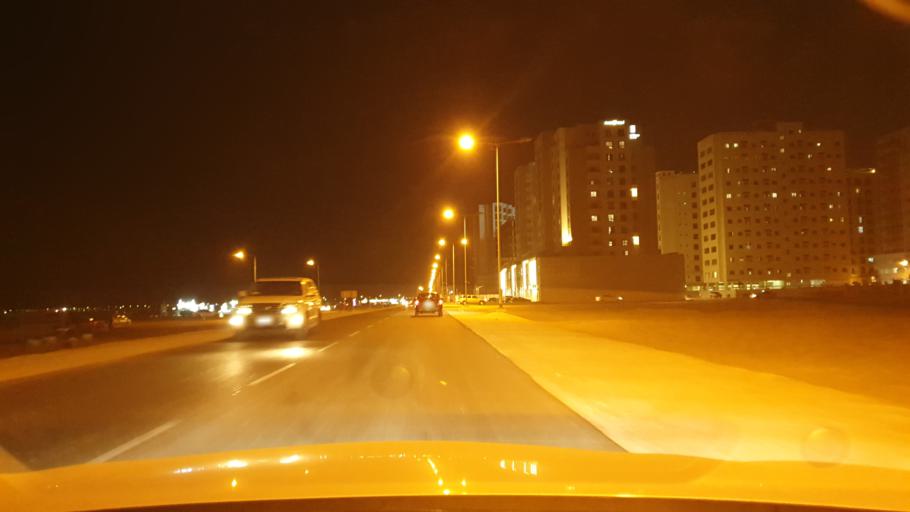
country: BH
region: Muharraq
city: Al Muharraq
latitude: 26.2618
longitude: 50.5945
